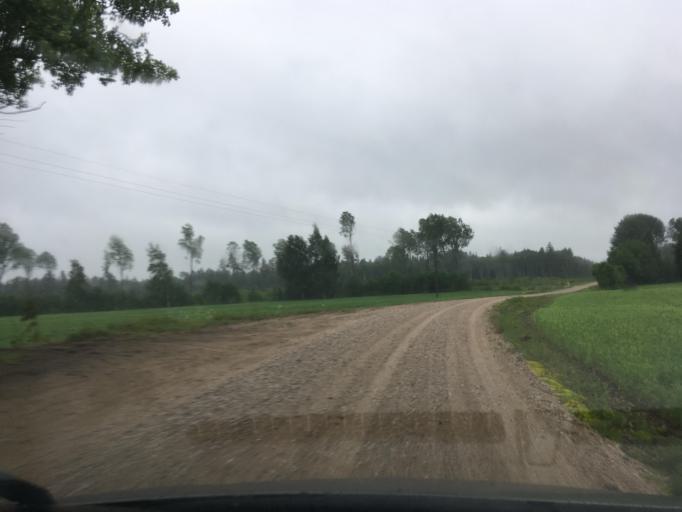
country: EE
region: Laeaene
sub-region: Lihula vald
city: Lihula
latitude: 58.6169
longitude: 23.8260
